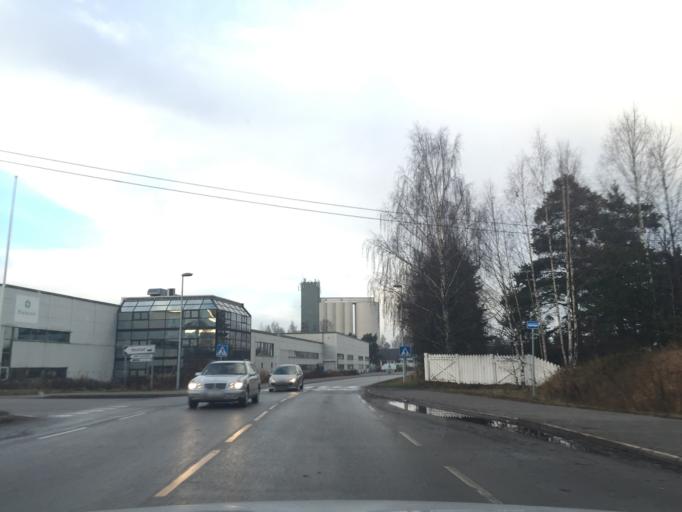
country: NO
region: Hedmark
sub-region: Elverum
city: Elverum
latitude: 60.8775
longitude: 11.5490
